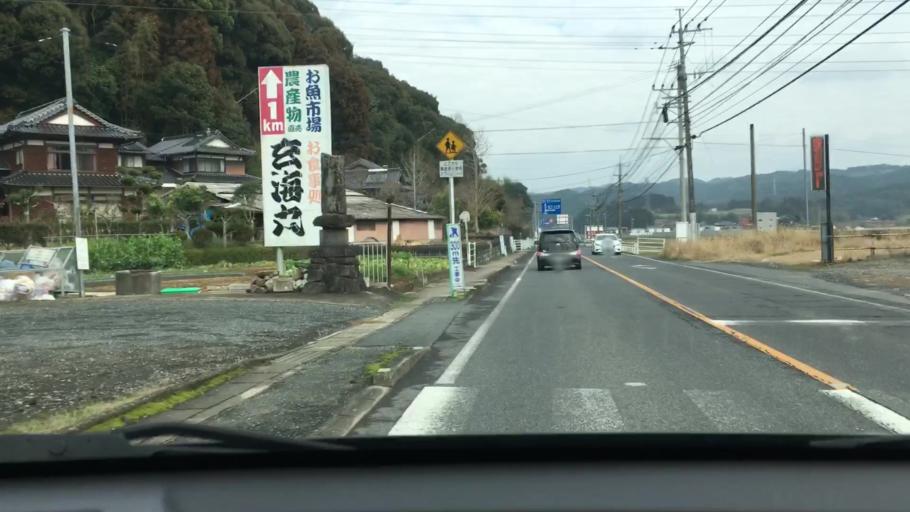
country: JP
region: Saga Prefecture
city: Imaricho-ko
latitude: 33.3043
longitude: 129.9226
